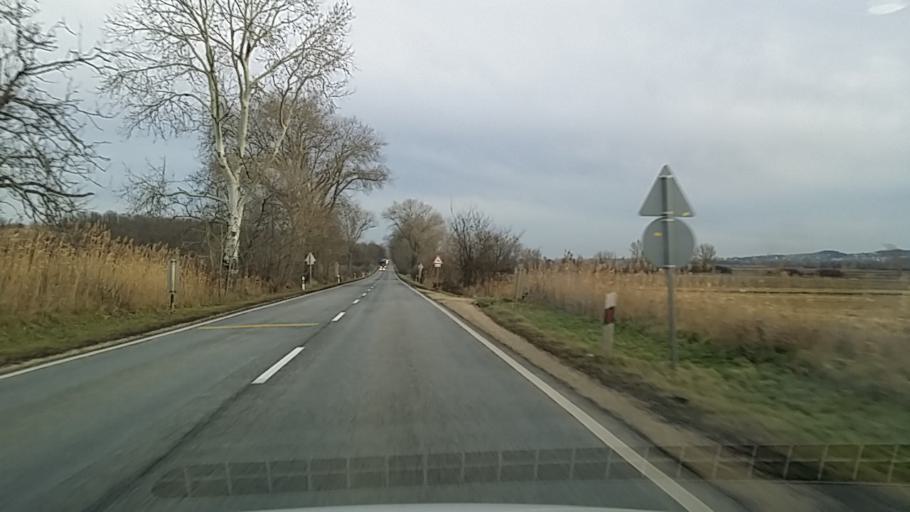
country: HU
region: Fejer
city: Mor
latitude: 47.3564
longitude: 18.2123
